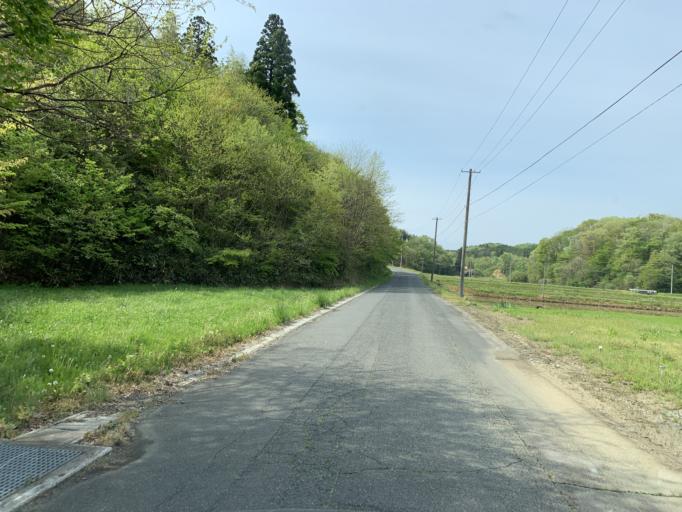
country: JP
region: Iwate
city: Ichinoseki
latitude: 38.8946
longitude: 141.0617
